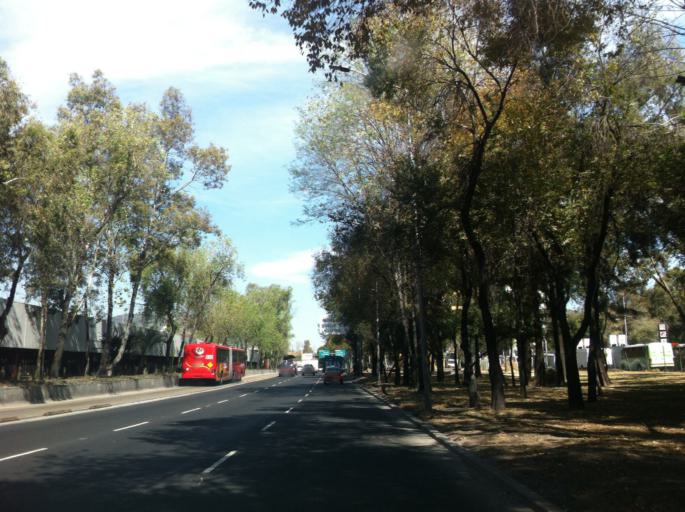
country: MX
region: Mexico
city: Colonia Lindavista
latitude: 19.4841
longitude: -99.1261
